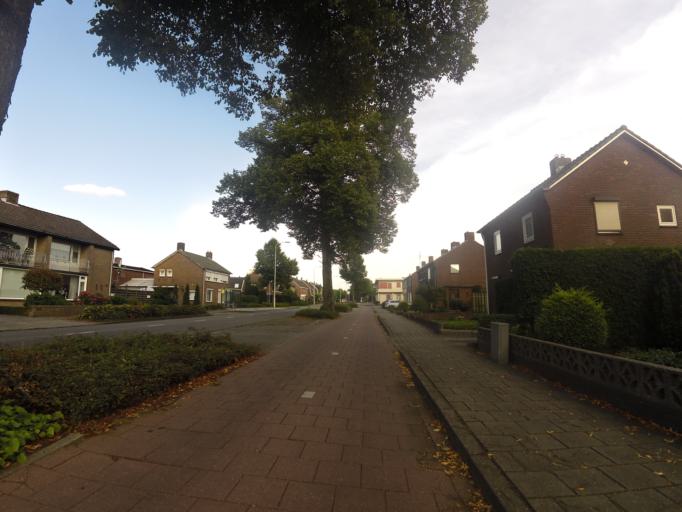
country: NL
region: Gelderland
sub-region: Oude IJsselstreek
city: Gendringen
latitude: 51.9270
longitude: 6.3519
